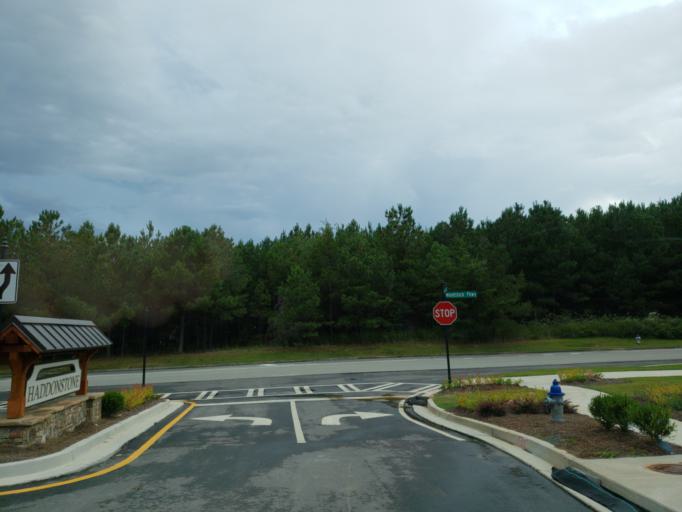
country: US
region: Georgia
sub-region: Cherokee County
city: Woodstock
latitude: 34.1071
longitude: -84.5304
